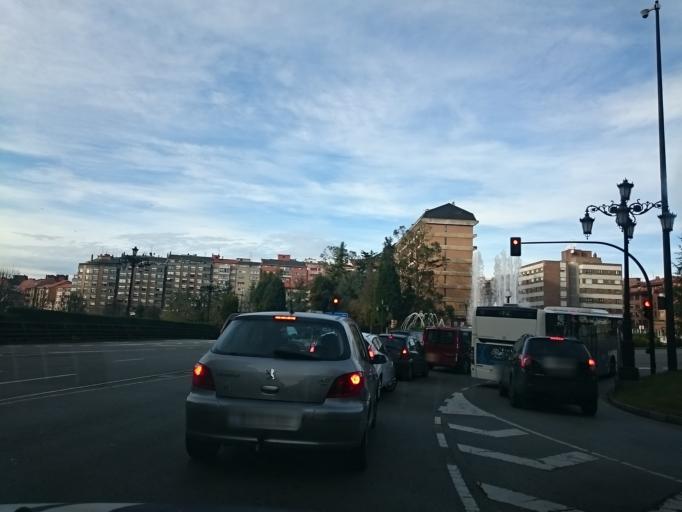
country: ES
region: Asturias
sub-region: Province of Asturias
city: Oviedo
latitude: 43.3601
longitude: -5.8497
